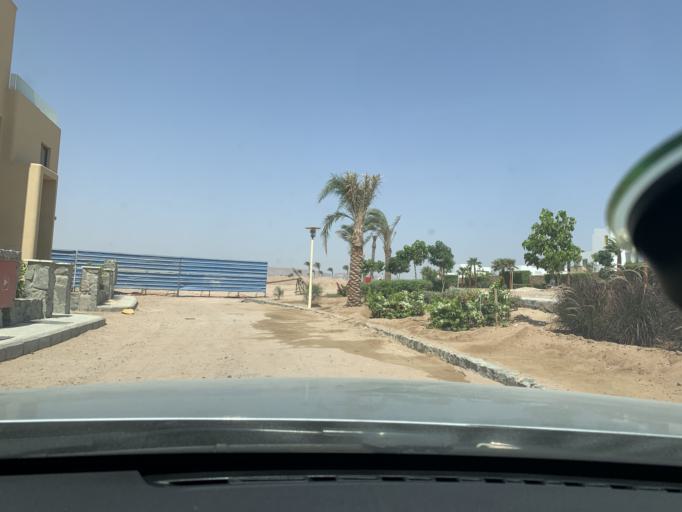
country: EG
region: Red Sea
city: El Gouna
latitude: 27.4037
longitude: 33.6588
